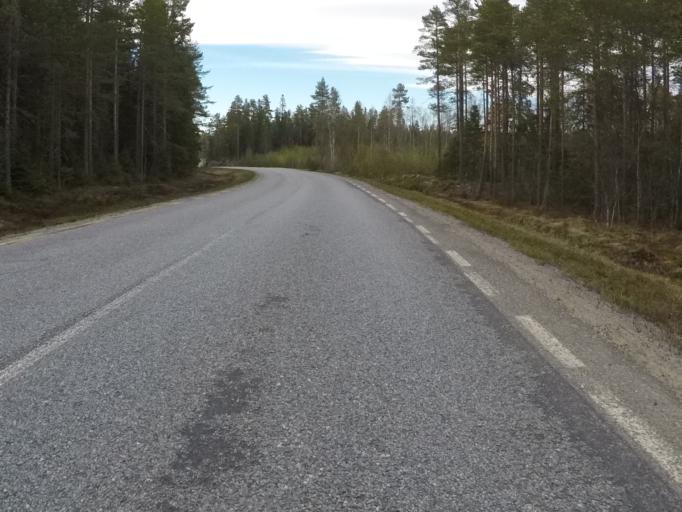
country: SE
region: Vaesterbotten
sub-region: Robertsfors Kommun
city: Robertsfors
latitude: 63.9837
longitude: 20.8122
